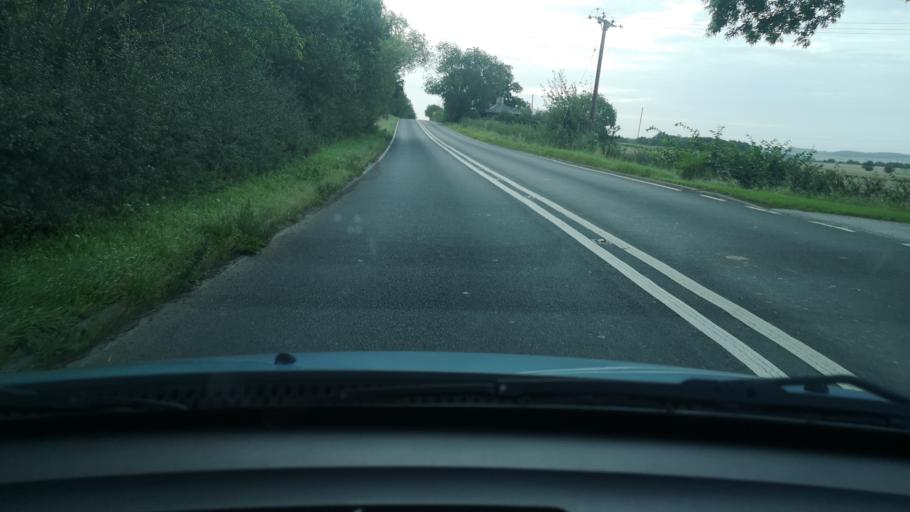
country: GB
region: England
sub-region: City and Borough of Wakefield
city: Badsworth
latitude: 53.6177
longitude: -1.3077
